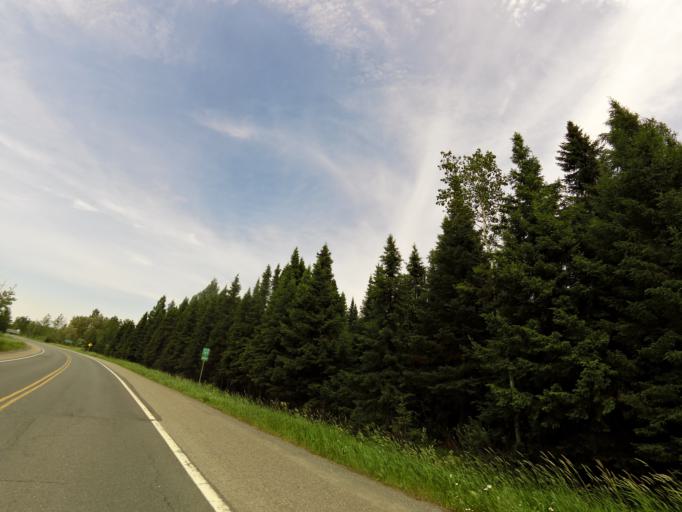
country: CA
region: Quebec
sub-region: Abitibi-Temiscamingue
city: Rouyn-Noranda
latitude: 47.9170
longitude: -79.2404
